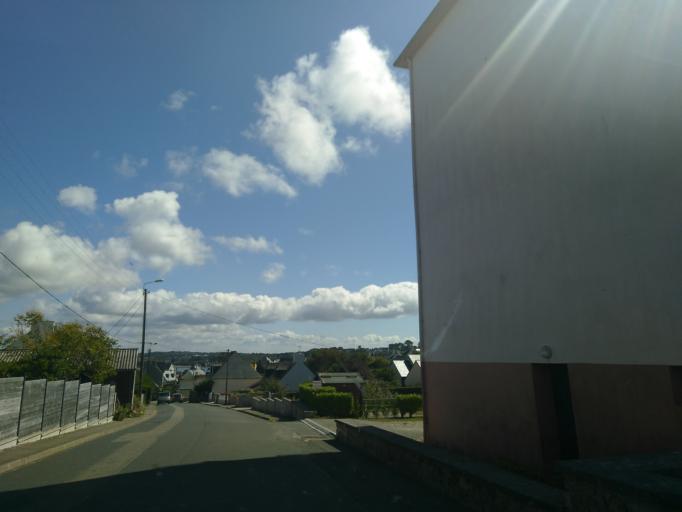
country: FR
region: Brittany
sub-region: Departement du Finistere
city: Camaret-sur-Mer
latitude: 48.2793
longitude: -4.6033
